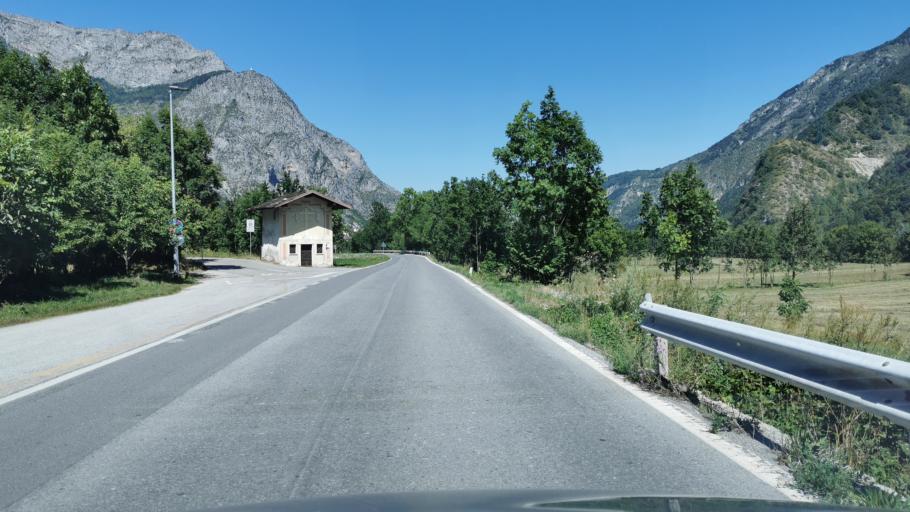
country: IT
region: Piedmont
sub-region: Provincia di Cuneo
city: Valdieri
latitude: 44.2673
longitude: 7.3870
